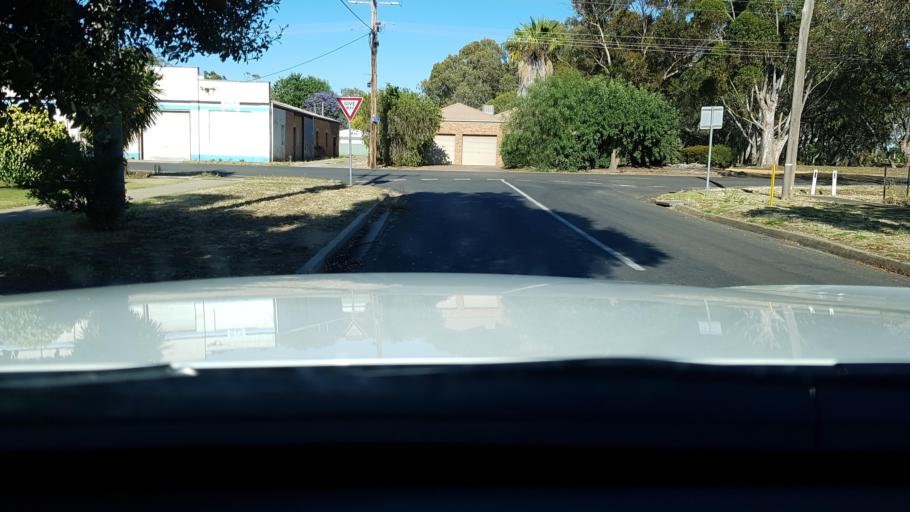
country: AU
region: Victoria
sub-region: Horsham
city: Horsham
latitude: -36.2448
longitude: 142.3950
